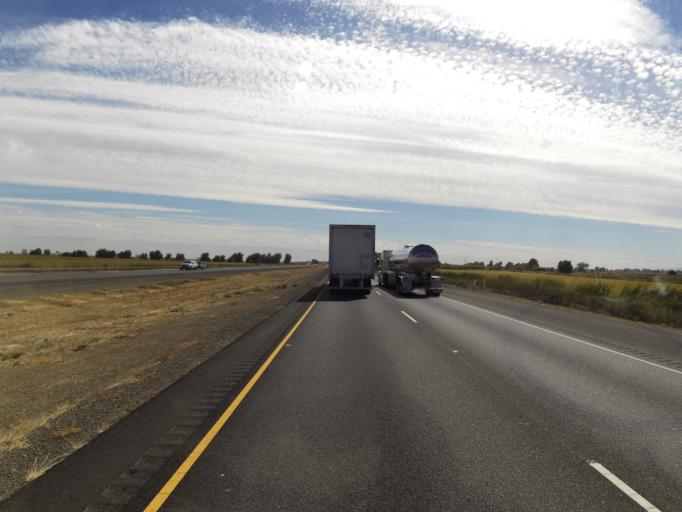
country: US
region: California
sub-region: Colusa County
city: Williams
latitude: 39.1822
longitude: -122.1637
